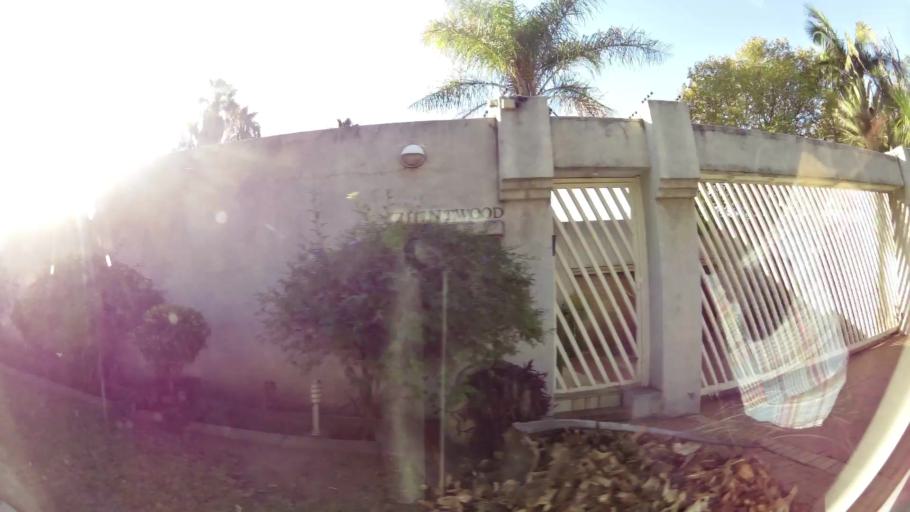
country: ZA
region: Gauteng
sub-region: City of Johannesburg Metropolitan Municipality
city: Johannesburg
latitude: -26.1136
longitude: 28.0674
